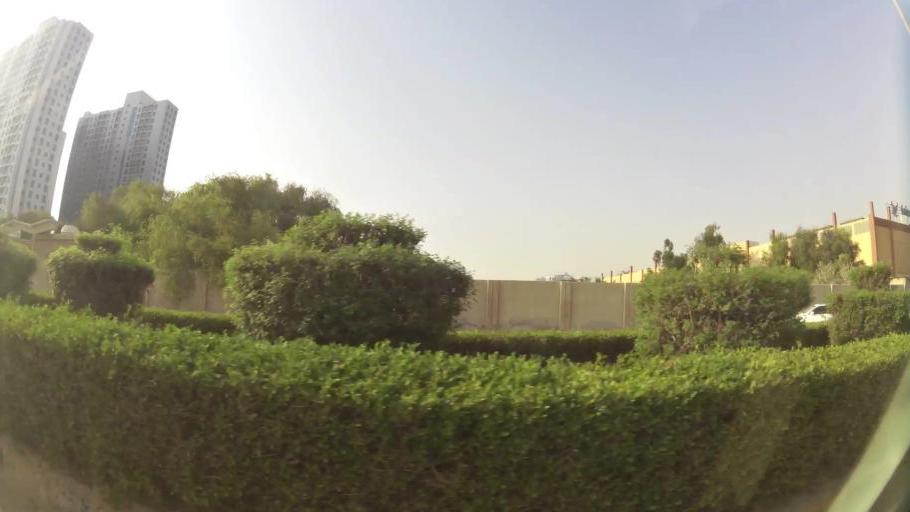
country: AE
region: Ajman
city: Ajman
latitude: 25.3894
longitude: 55.4438
